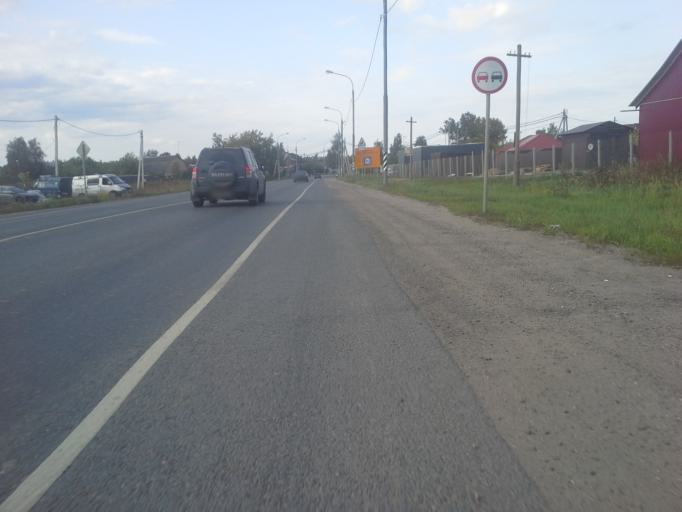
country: RU
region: Moskovskaya
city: Golitsyno
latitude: 55.5911
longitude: 37.0038
